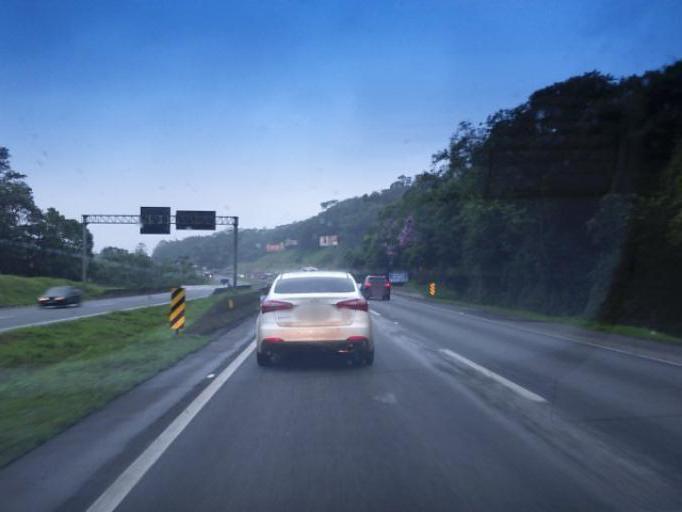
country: BR
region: Santa Catarina
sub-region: Joinville
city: Joinville
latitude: -26.0029
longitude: -48.8733
